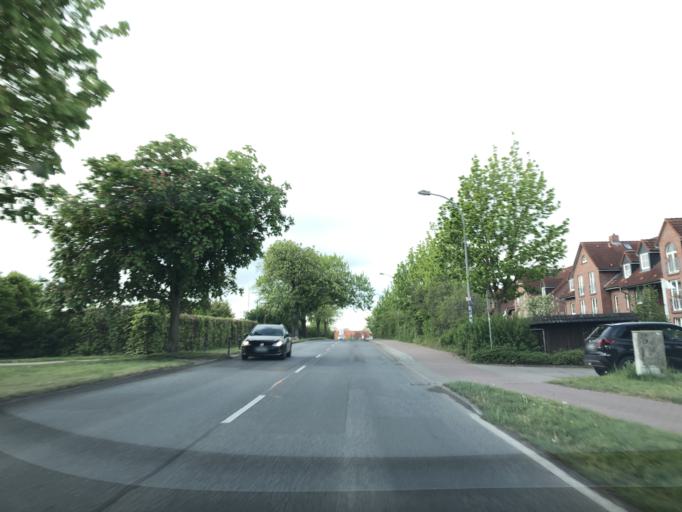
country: DE
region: Mecklenburg-Vorpommern
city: Guestrow
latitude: 53.7767
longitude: 12.1724
